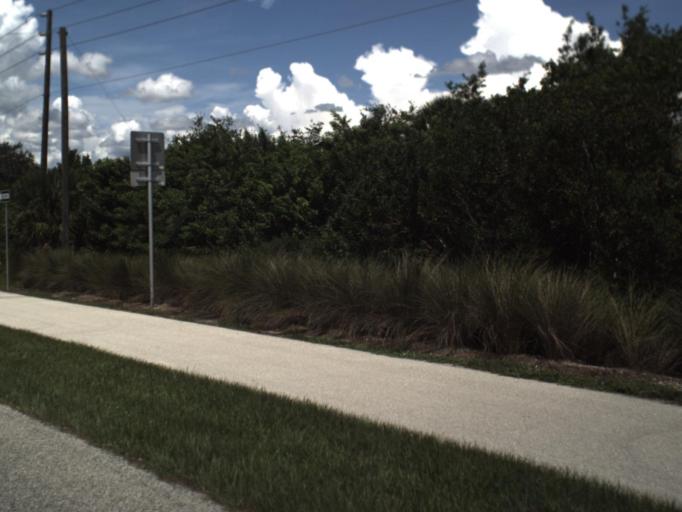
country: US
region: Florida
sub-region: Charlotte County
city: Charlotte Park
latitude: 26.9028
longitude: -82.0344
